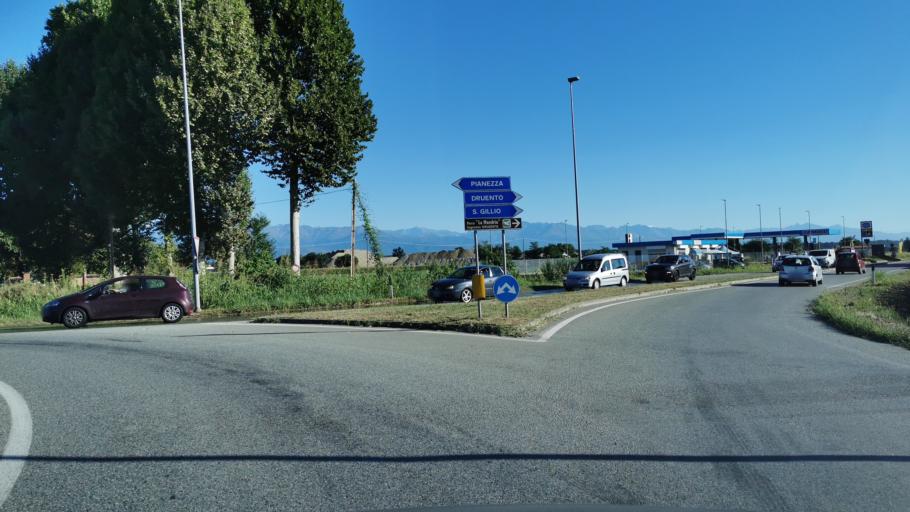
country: IT
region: Piedmont
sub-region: Provincia di Torino
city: Druento
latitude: 45.1171
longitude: 7.5903
